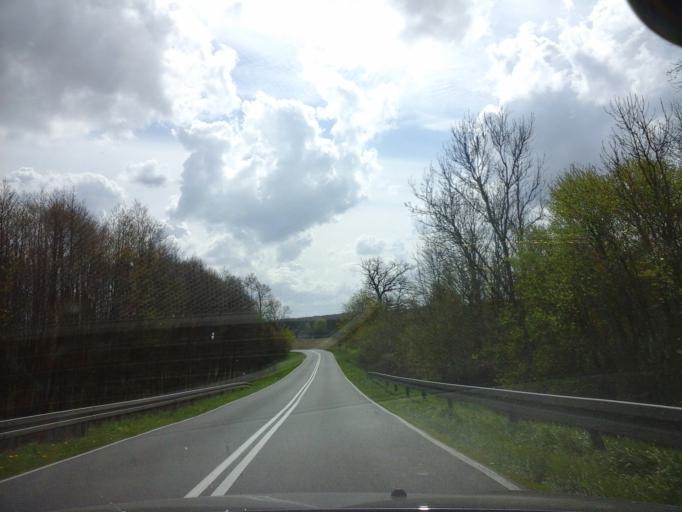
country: PL
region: West Pomeranian Voivodeship
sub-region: Powiat stargardzki
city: Suchan
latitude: 53.2579
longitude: 15.3330
